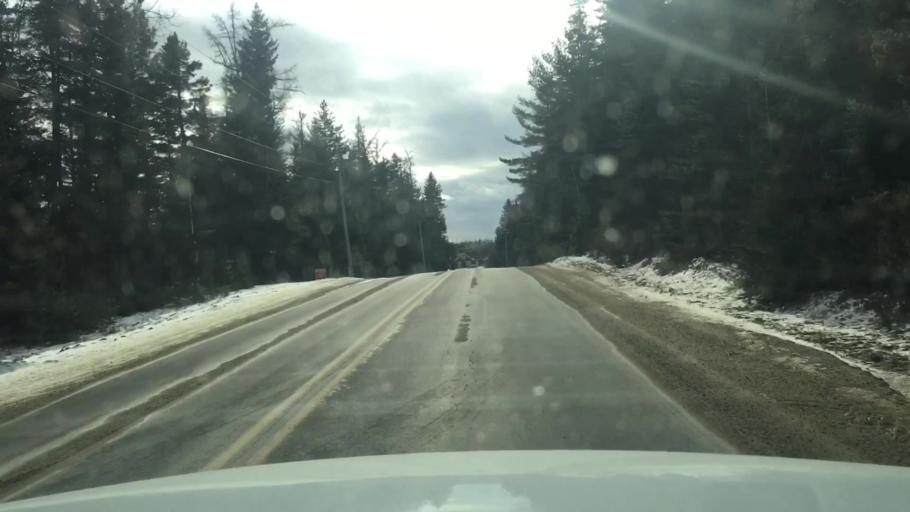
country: US
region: Maine
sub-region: Washington County
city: Jonesport
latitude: 44.6327
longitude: -67.5945
